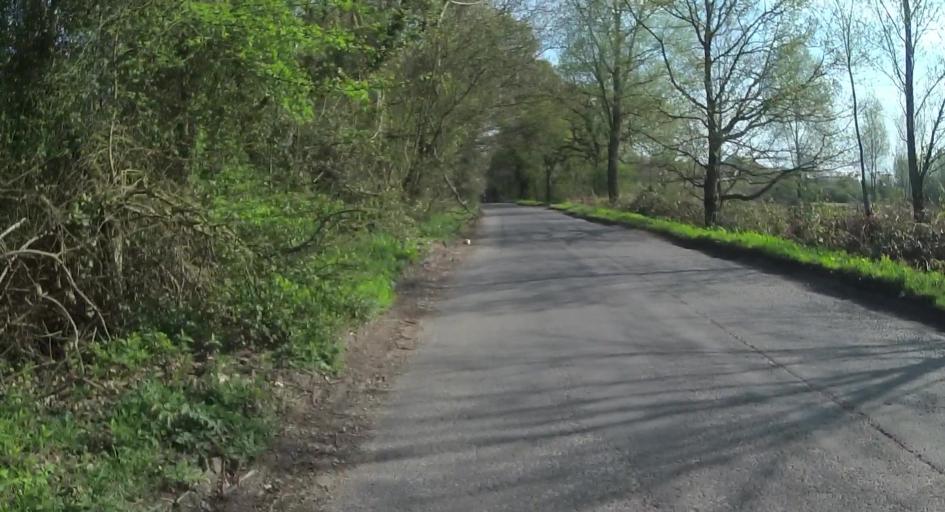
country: GB
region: England
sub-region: West Berkshire
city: Stratfield Mortimer
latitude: 51.3427
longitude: -1.0679
